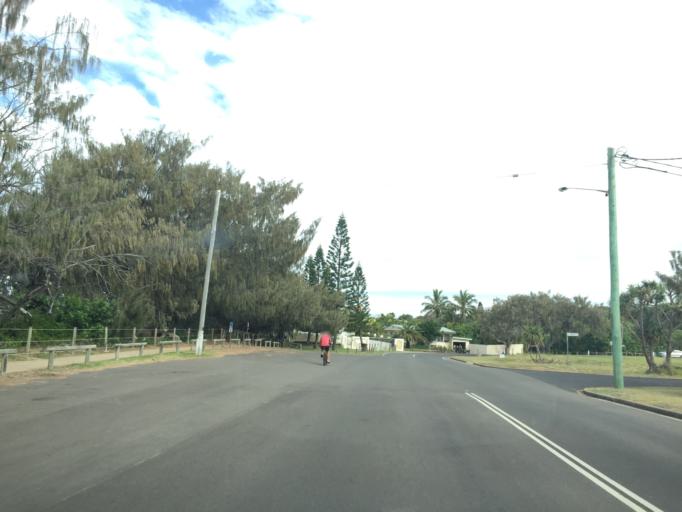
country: AU
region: Queensland
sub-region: Bundaberg
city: Bundaberg
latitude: -24.8285
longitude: 152.4671
